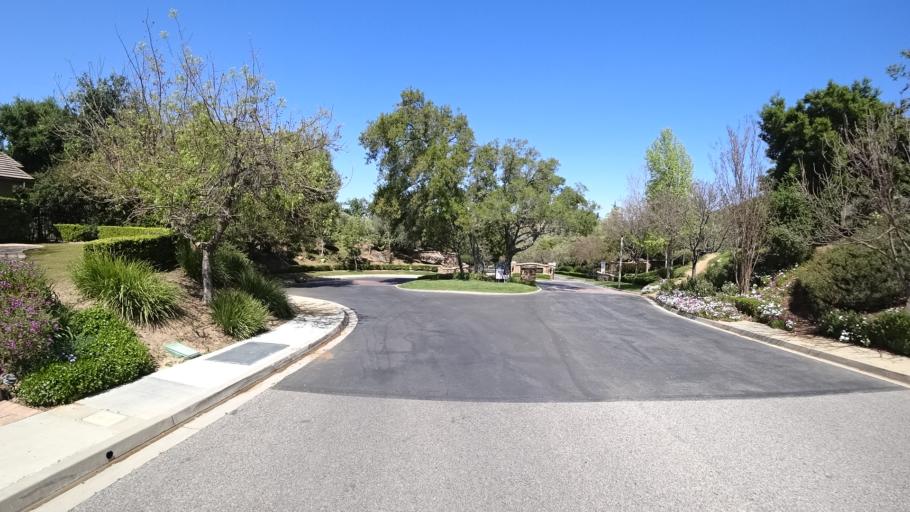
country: US
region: California
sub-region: Ventura County
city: Casa Conejo
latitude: 34.2051
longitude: -118.8992
